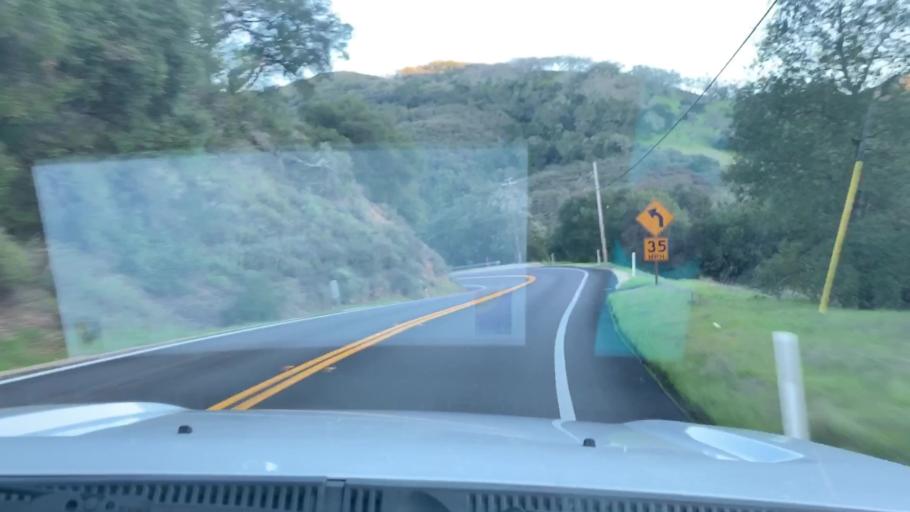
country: US
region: California
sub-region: San Luis Obispo County
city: Atascadero
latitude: 35.4510
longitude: -120.7009
